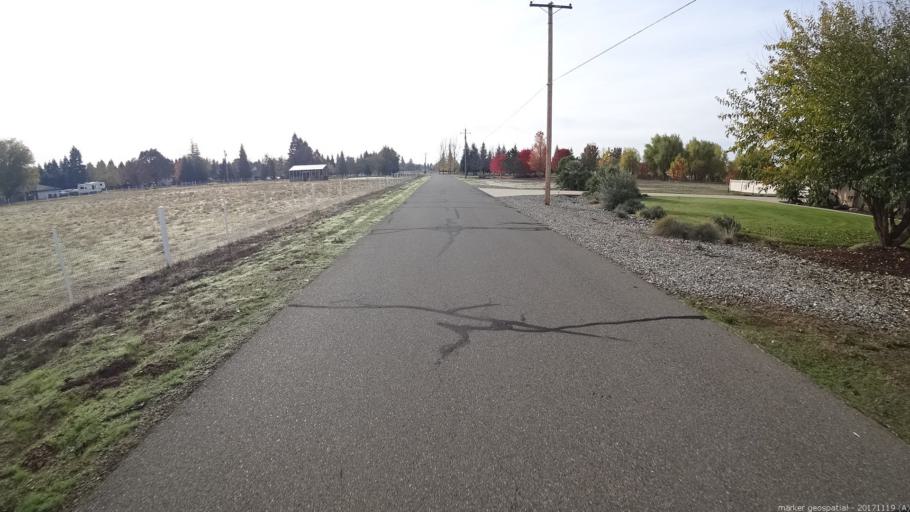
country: US
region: California
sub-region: Shasta County
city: Anderson
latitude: 40.5103
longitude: -122.3293
